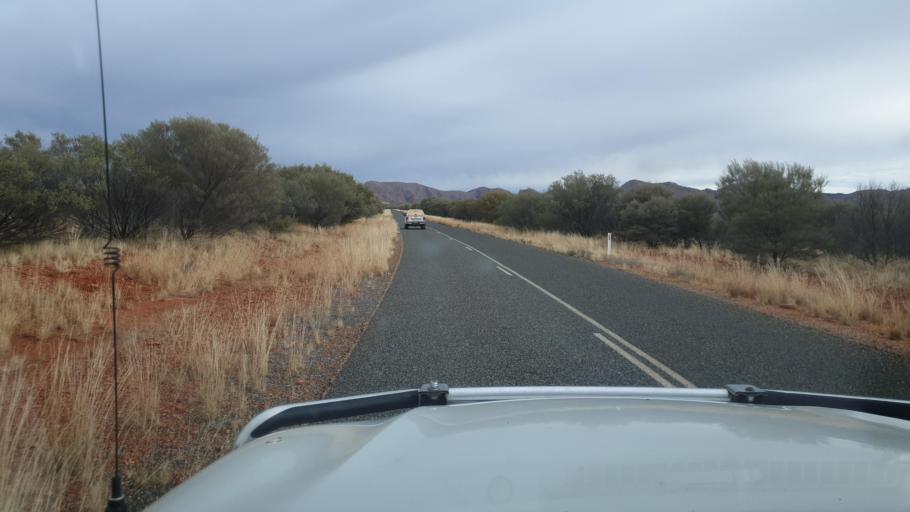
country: AU
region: Northern Territory
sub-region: Alice Springs
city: Alice Springs
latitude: -23.7620
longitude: 133.5002
